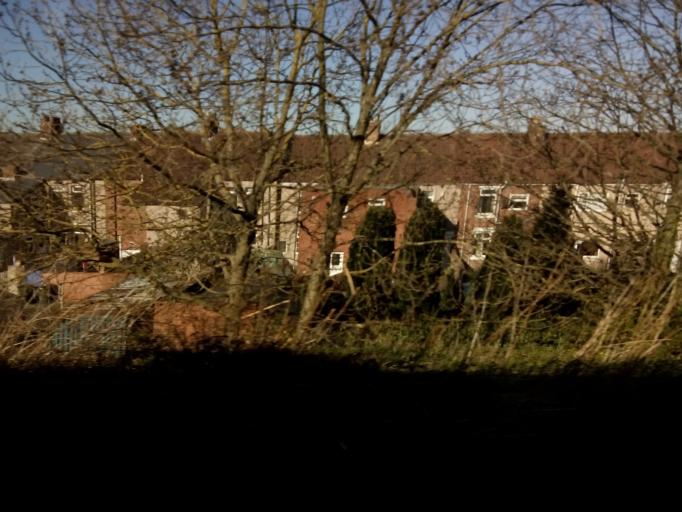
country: GB
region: England
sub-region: Northumberland
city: Cramlington
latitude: 55.0559
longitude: -1.5968
